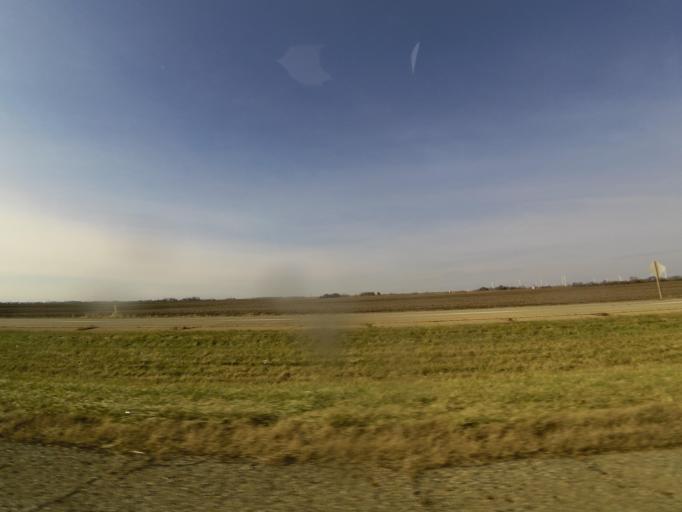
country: US
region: Illinois
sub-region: Macon County
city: Forsyth
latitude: 39.9516
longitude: -88.9554
